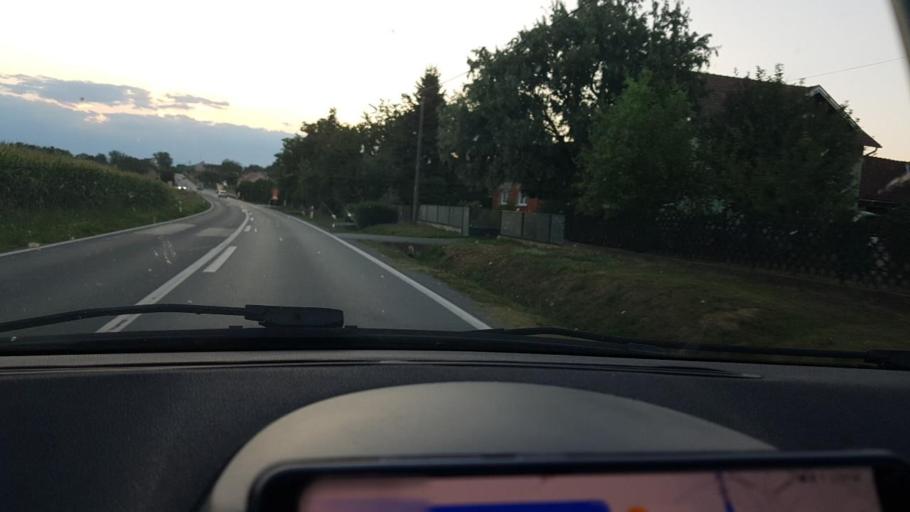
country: HR
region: Bjelovarsko-Bilogorska
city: Zdralovi
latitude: 45.8699
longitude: 16.9024
